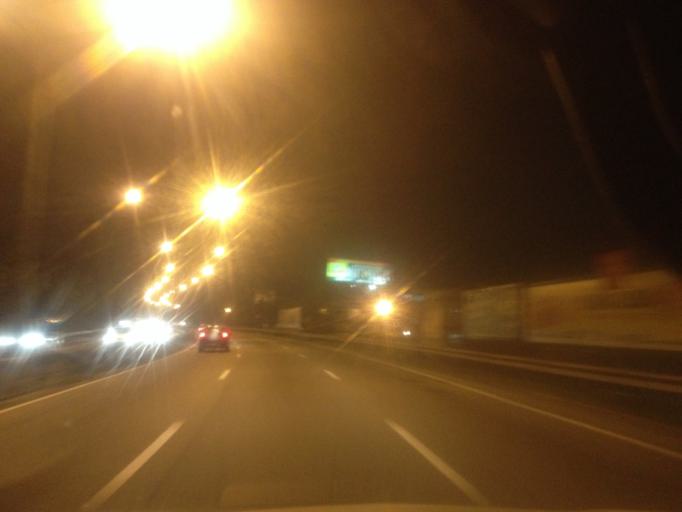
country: BR
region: Rio de Janeiro
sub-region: Duque De Caxias
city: Duque de Caxias
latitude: -22.8006
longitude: -43.3258
